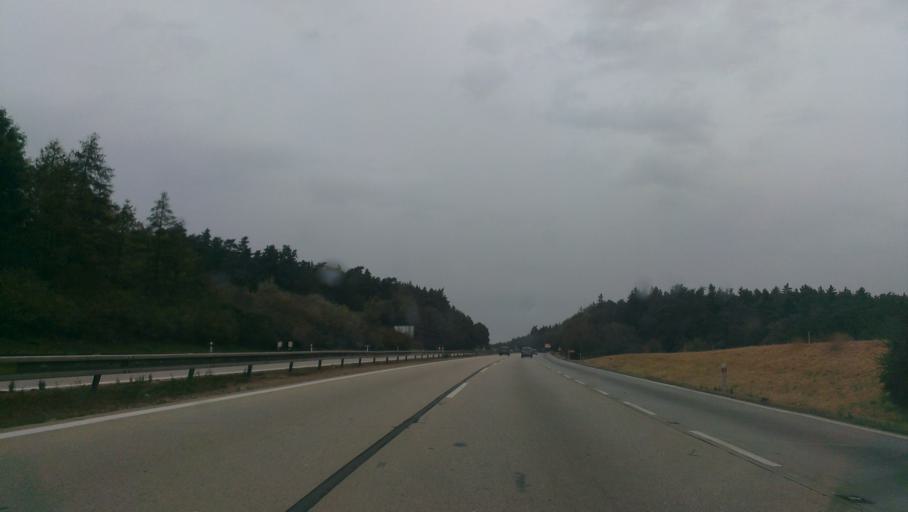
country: CZ
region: South Moravian
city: Ricany
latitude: 49.2274
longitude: 16.3864
